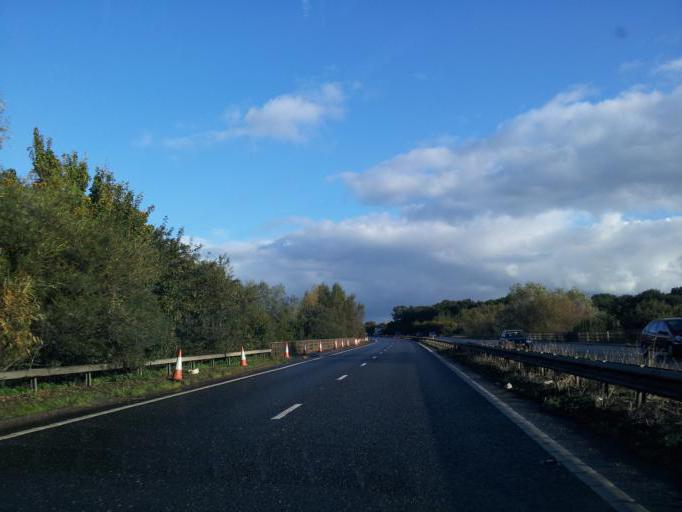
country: GB
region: England
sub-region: Norfolk
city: Bowthorpe
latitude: 52.6322
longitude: 1.1954
